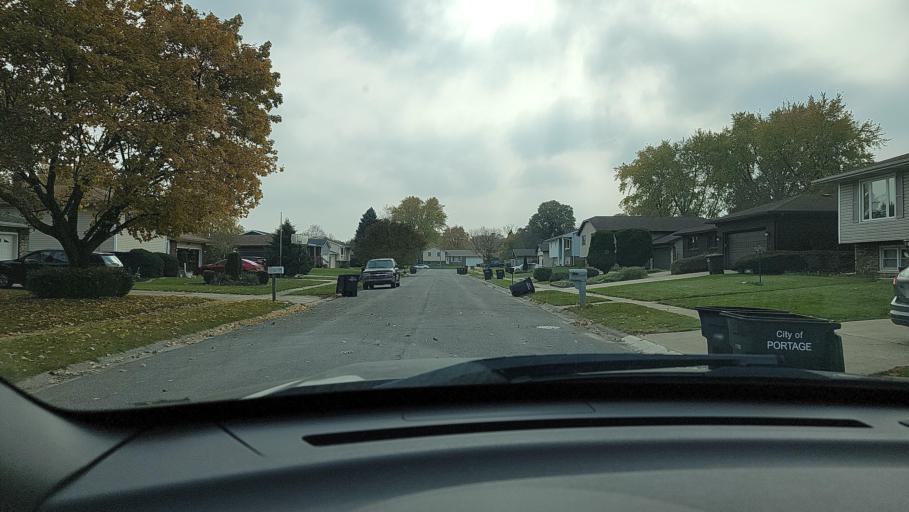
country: US
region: Indiana
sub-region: Porter County
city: Portage
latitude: 41.5914
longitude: -87.1569
